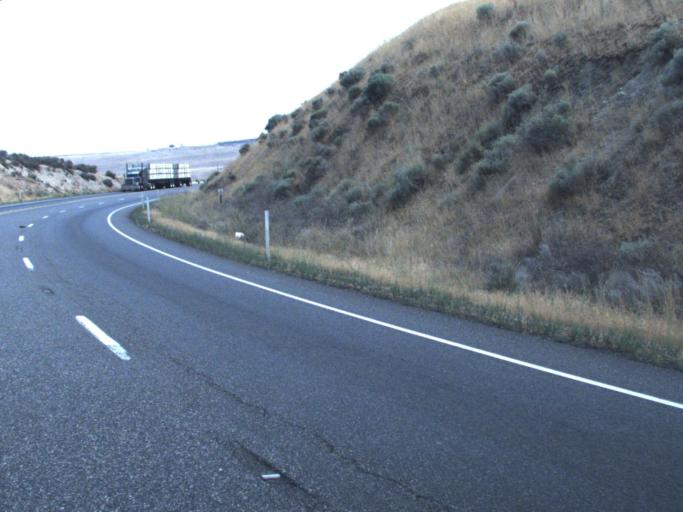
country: US
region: Washington
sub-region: Benton County
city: Prosser
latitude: 46.2087
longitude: -119.7287
